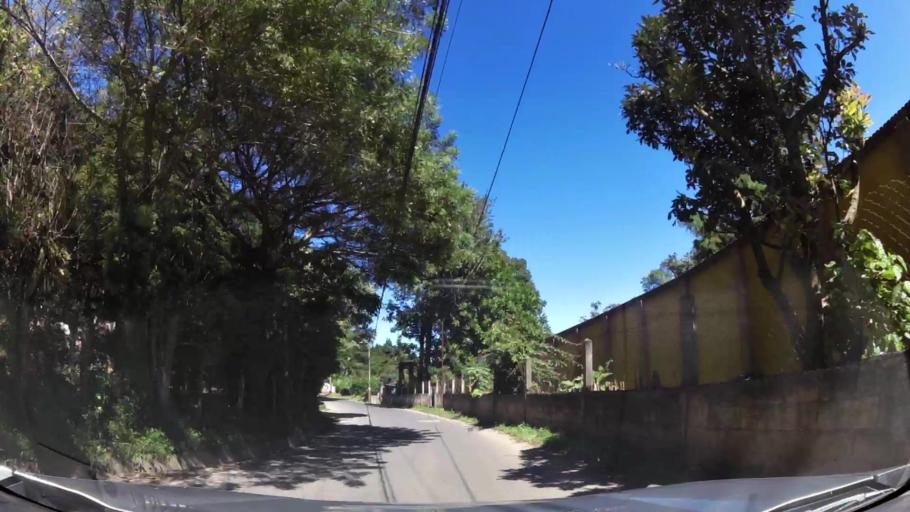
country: GT
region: Guatemala
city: San Jose Pinula
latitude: 14.5341
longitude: -90.4150
